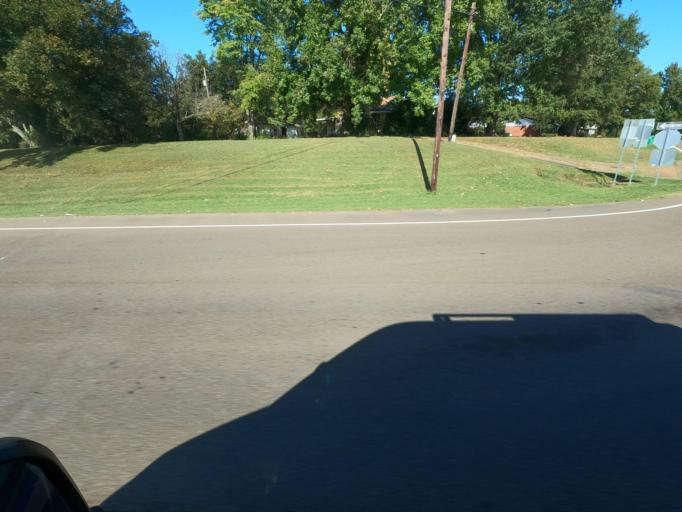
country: US
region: Tennessee
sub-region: Tipton County
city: Munford
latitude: 35.4216
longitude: -89.8187
